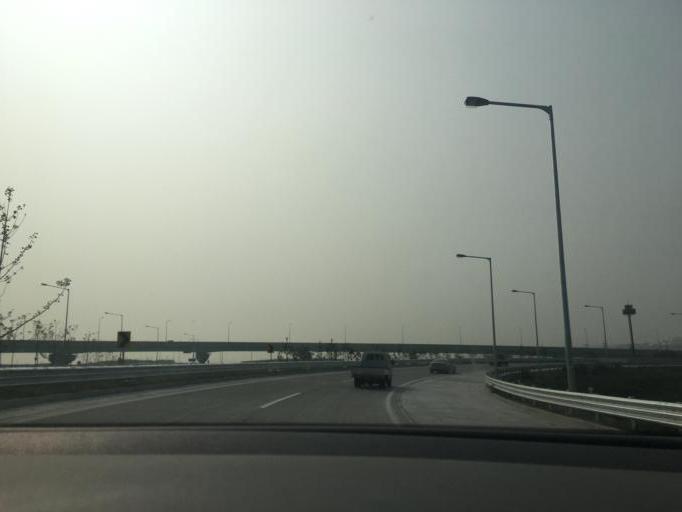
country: KR
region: Gyeonggi-do
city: Guri-si
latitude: 37.5784
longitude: 127.1363
